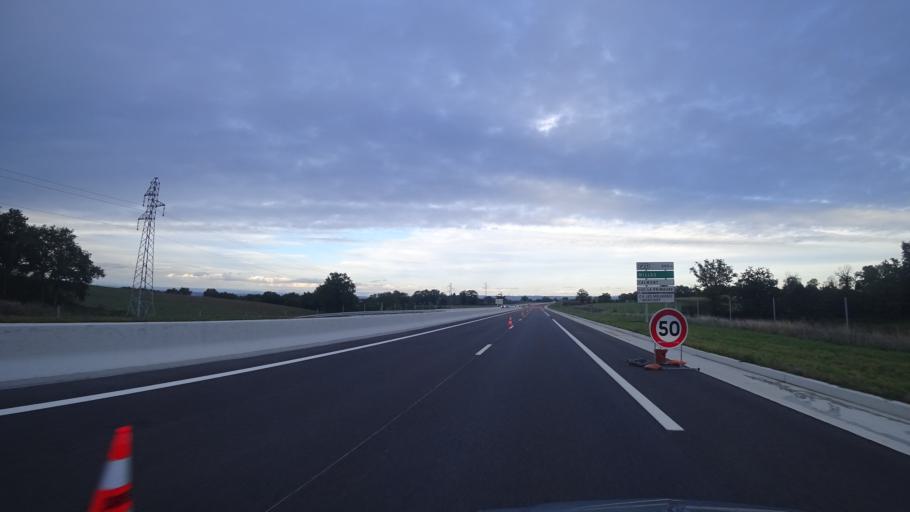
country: FR
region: Midi-Pyrenees
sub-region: Departement de l'Aveyron
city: Calmont
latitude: 44.2903
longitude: 2.4949
